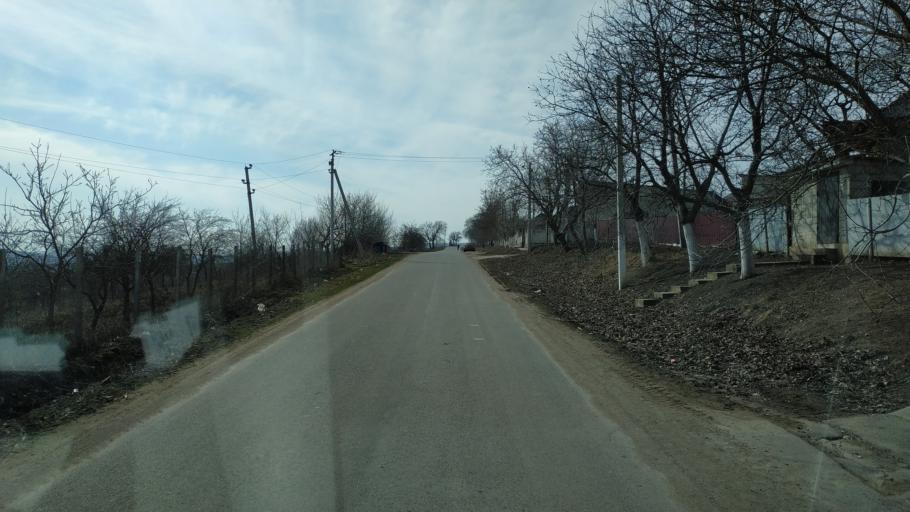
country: MD
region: Nisporeni
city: Nisporeni
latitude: 47.1529
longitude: 28.1299
